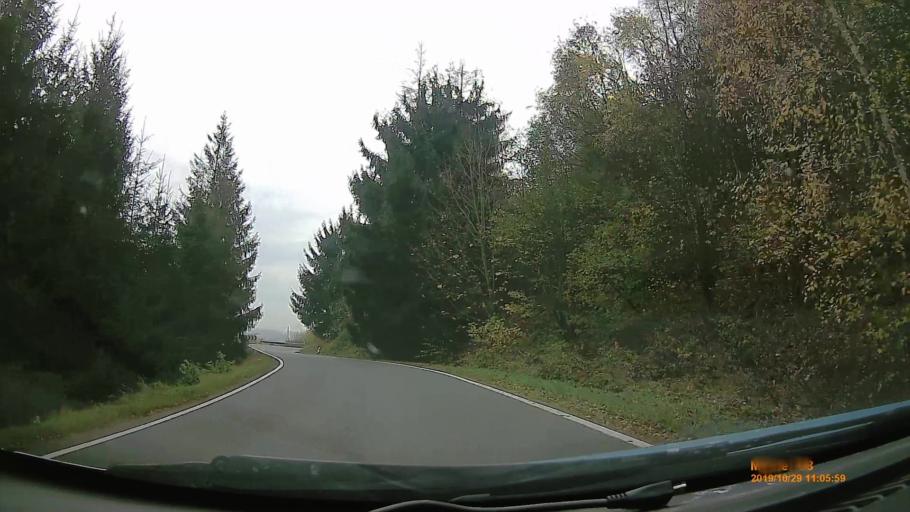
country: PL
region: Lower Silesian Voivodeship
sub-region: Powiat klodzki
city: Szczytna
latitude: 50.4665
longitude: 16.4787
